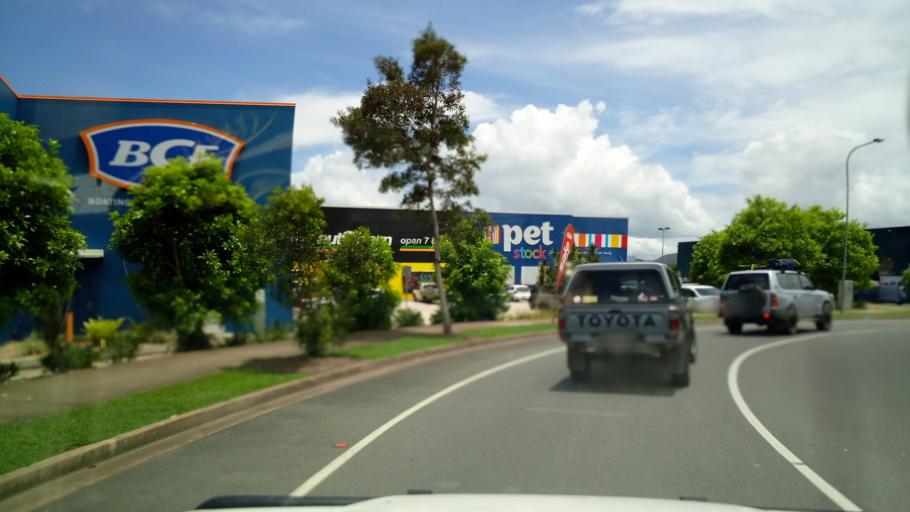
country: AU
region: Queensland
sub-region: Cairns
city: Redlynch
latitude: -16.8397
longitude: 145.6948
